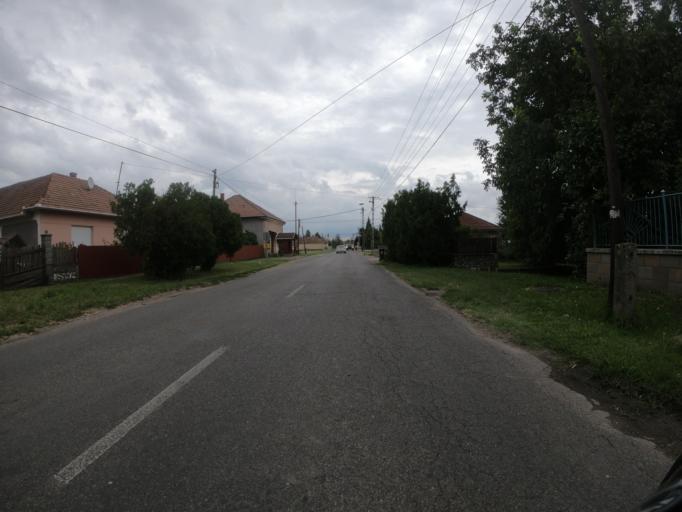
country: HU
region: Borsod-Abauj-Zemplen
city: Szentistvan
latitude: 47.7790
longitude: 20.6502
